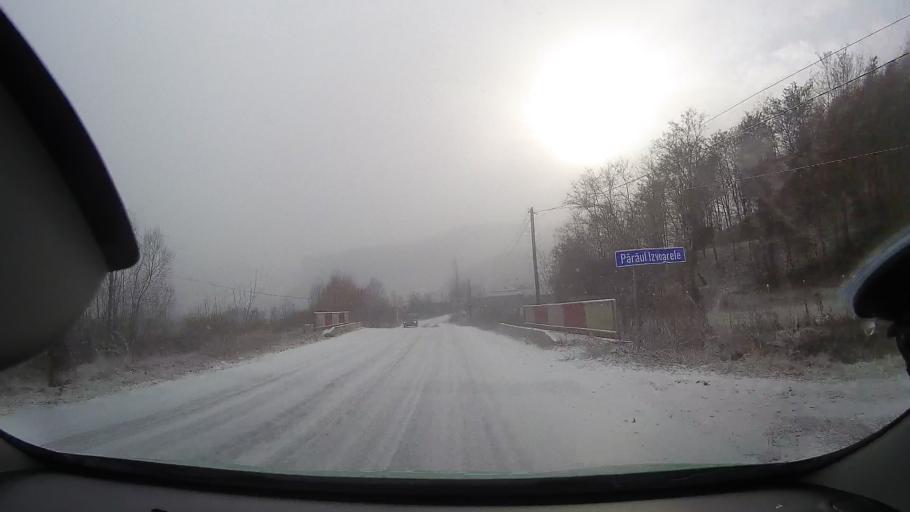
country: RO
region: Alba
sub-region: Comuna Rimetea
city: Rimetea
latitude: 46.3932
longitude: 23.5607
